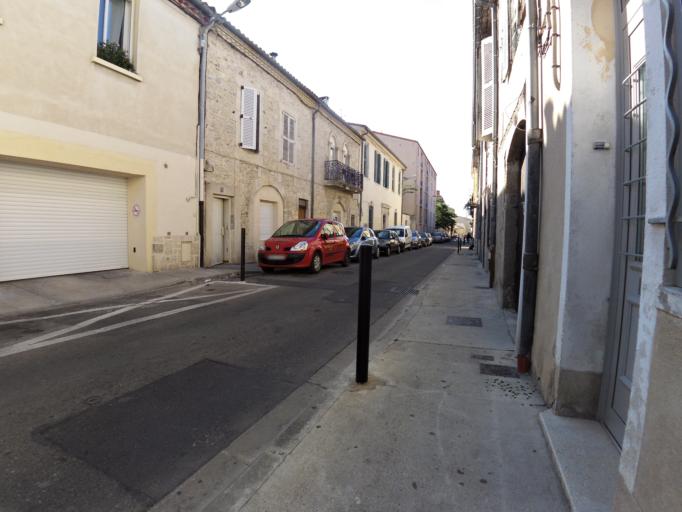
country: FR
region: Languedoc-Roussillon
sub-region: Departement du Gard
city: Nimes
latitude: 43.8306
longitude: 4.3580
